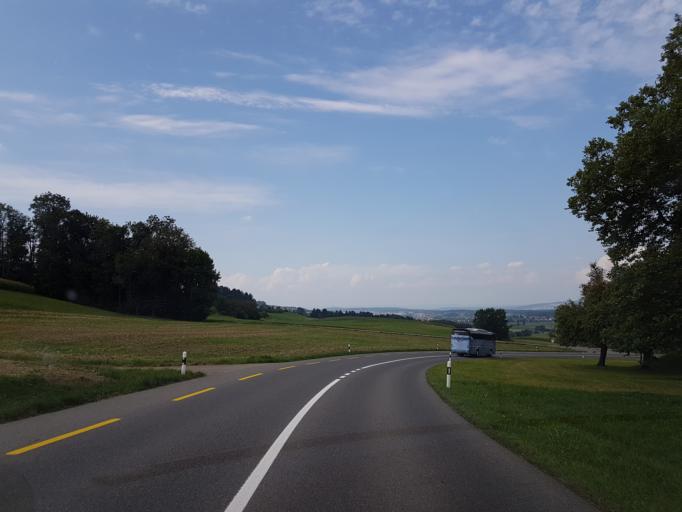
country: CH
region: Aargau
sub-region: Bezirk Muri
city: Muri
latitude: 47.2722
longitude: 8.3278
